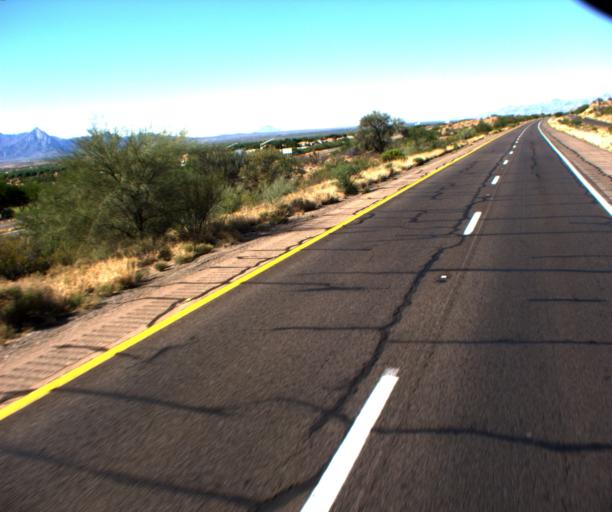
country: US
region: Arizona
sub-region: Pima County
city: Green Valley
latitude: 31.8303
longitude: -111.0017
